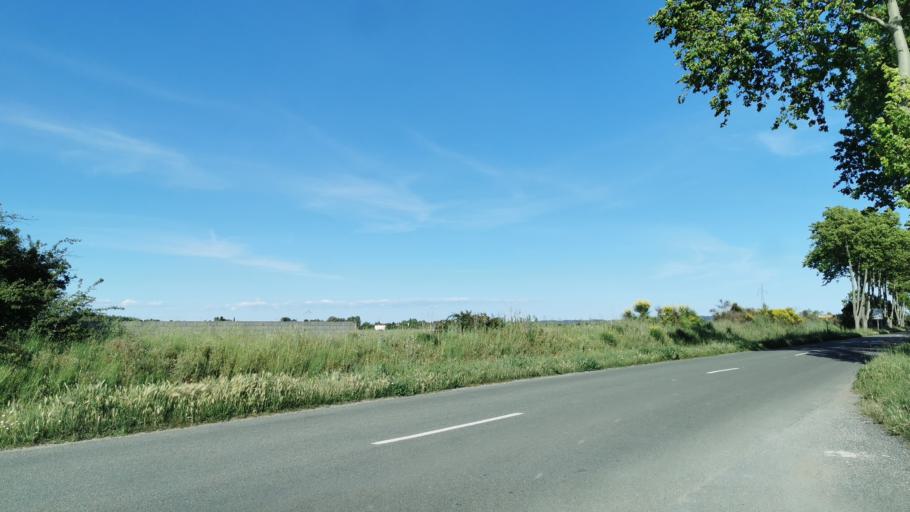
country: FR
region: Languedoc-Roussillon
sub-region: Departement de l'Aude
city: Canet
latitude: 43.2189
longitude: 2.8461
